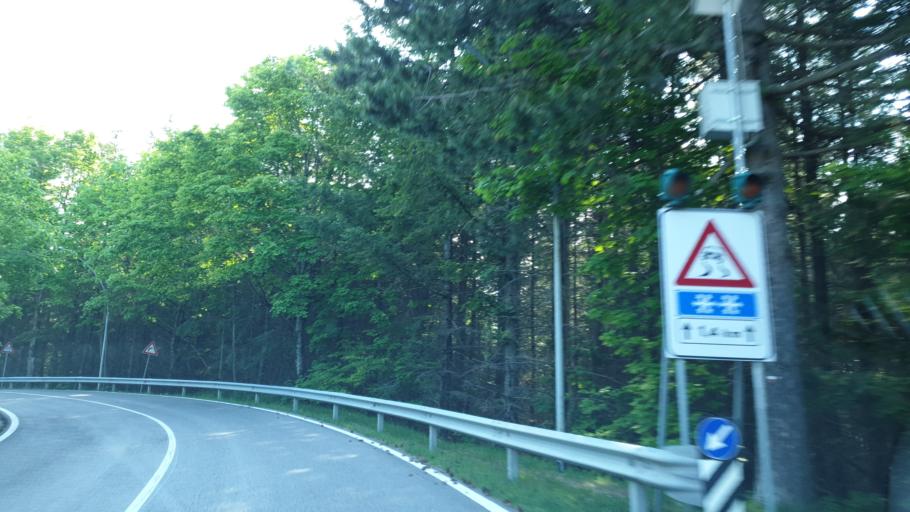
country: IT
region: Tuscany
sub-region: Province of Arezzo
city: Montemignaio
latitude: 43.7797
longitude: 11.5930
